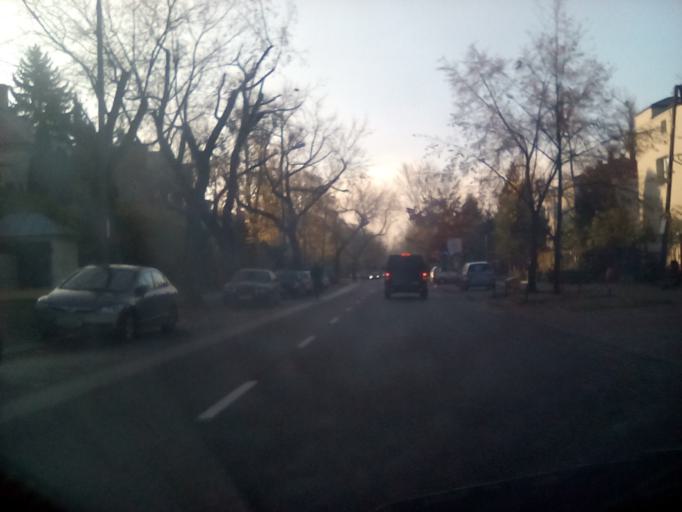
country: PL
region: Masovian Voivodeship
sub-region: Warszawa
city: Mokotow
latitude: 52.1951
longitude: 21.0198
